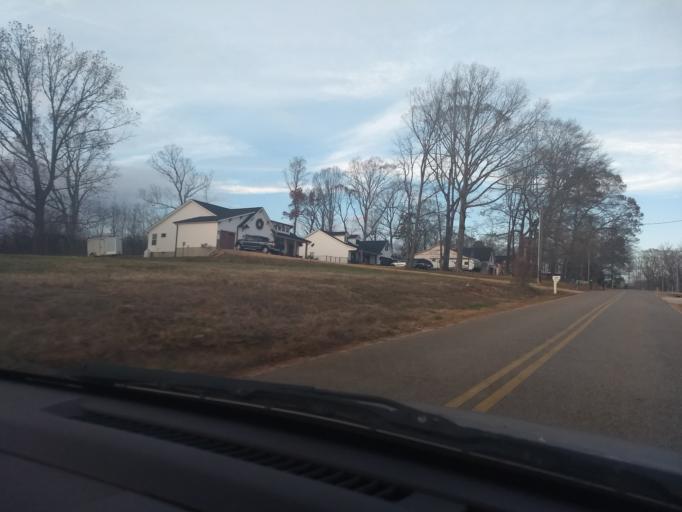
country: US
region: South Carolina
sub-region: Greenville County
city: Greer
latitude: 35.0219
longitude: -82.2029
